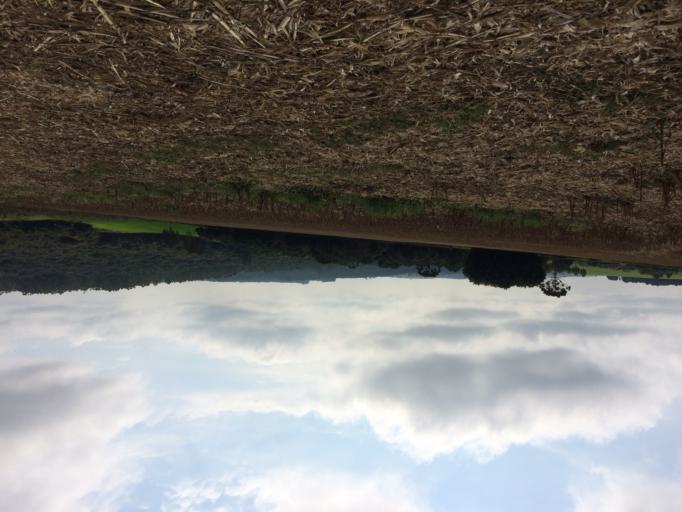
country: BR
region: Sao Paulo
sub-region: Capao Bonito
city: Capao Bonito
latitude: -23.9640
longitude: -48.2826
